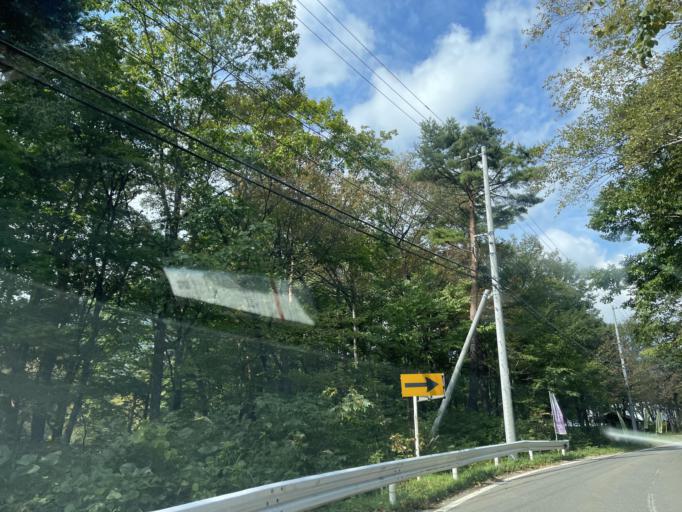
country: JP
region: Nagano
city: Omachi
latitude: 36.5222
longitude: 137.7998
